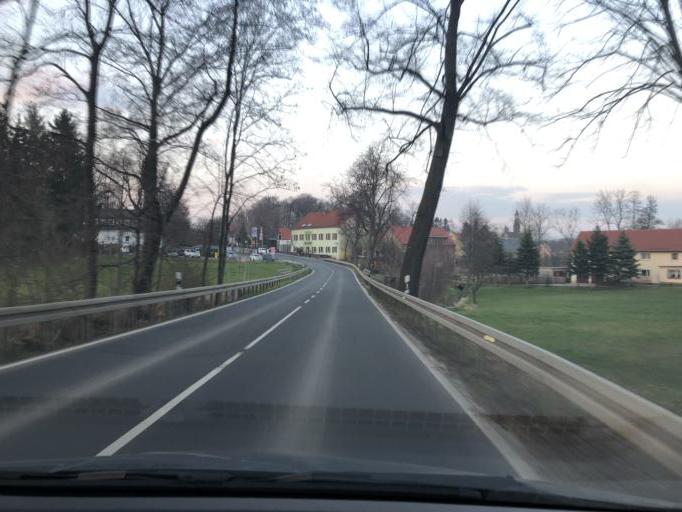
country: DE
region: Saxony
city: Elstra
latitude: 51.2338
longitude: 14.1300
